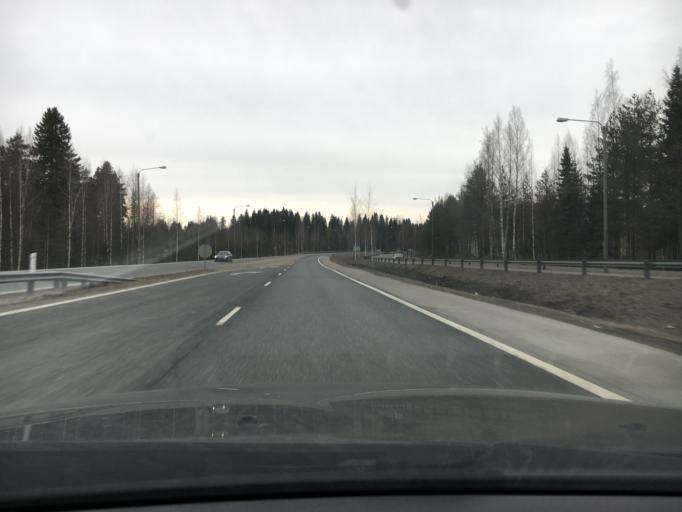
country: FI
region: Northern Savo
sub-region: Kuopio
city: Siilinjaervi
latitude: 63.0812
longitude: 27.6478
